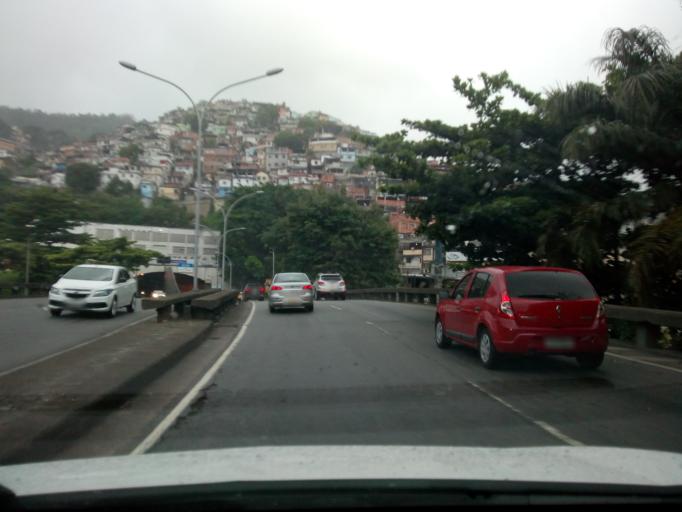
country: BR
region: Rio de Janeiro
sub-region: Rio De Janeiro
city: Rio de Janeiro
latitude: -22.9193
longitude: -43.1945
